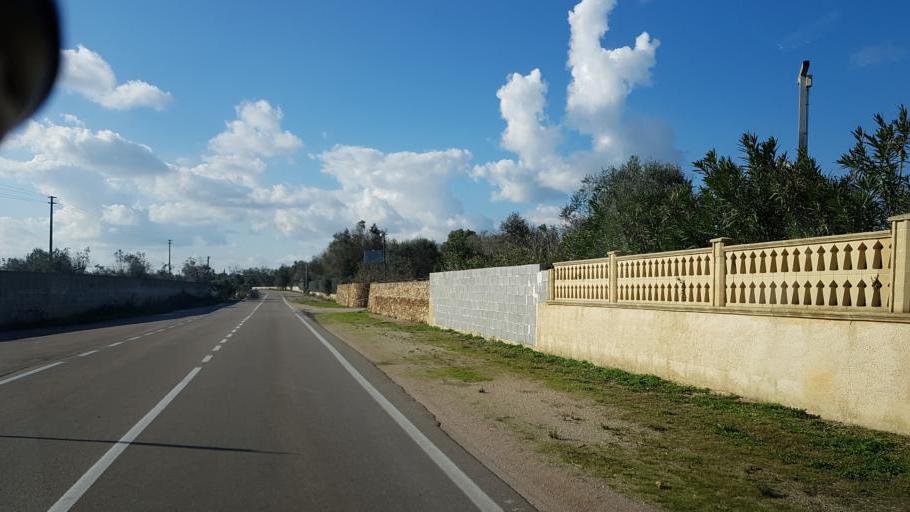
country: IT
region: Apulia
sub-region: Provincia di Lecce
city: Trepuzzi
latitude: 40.4425
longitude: 18.0930
